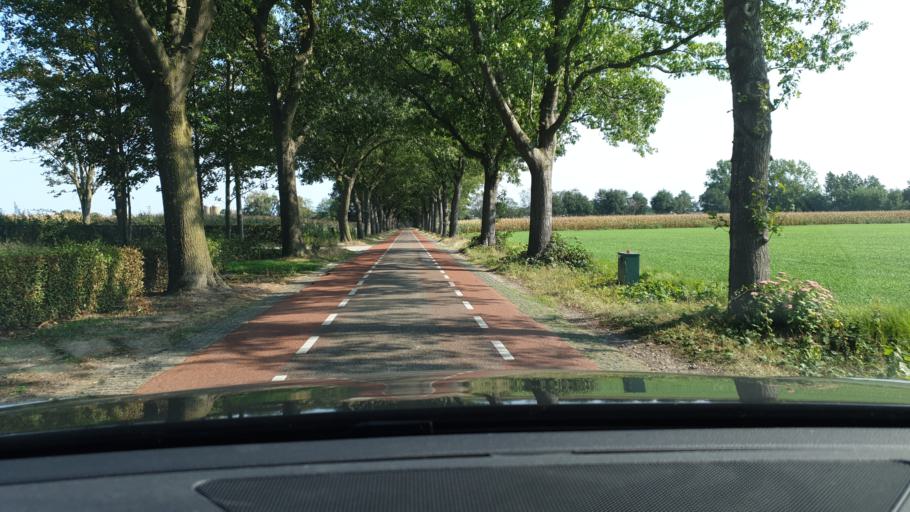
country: NL
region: North Brabant
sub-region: Gemeente Bernheze
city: Loosbroek
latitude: 51.7046
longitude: 5.5081
